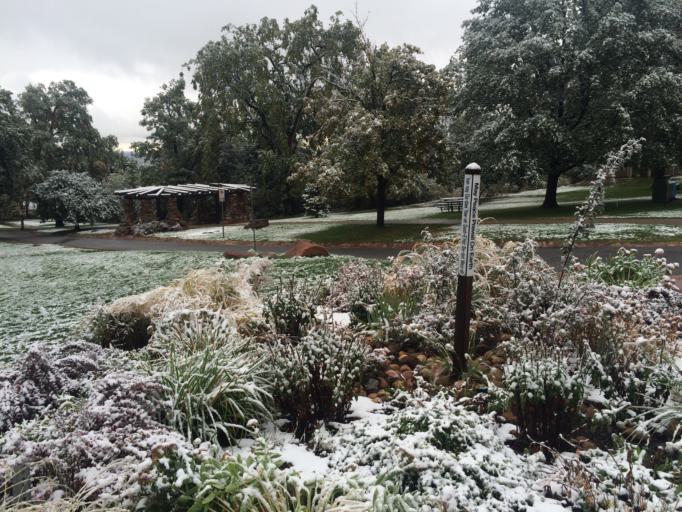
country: US
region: Colorado
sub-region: Boulder County
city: Boulder
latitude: 39.9987
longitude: -105.2806
